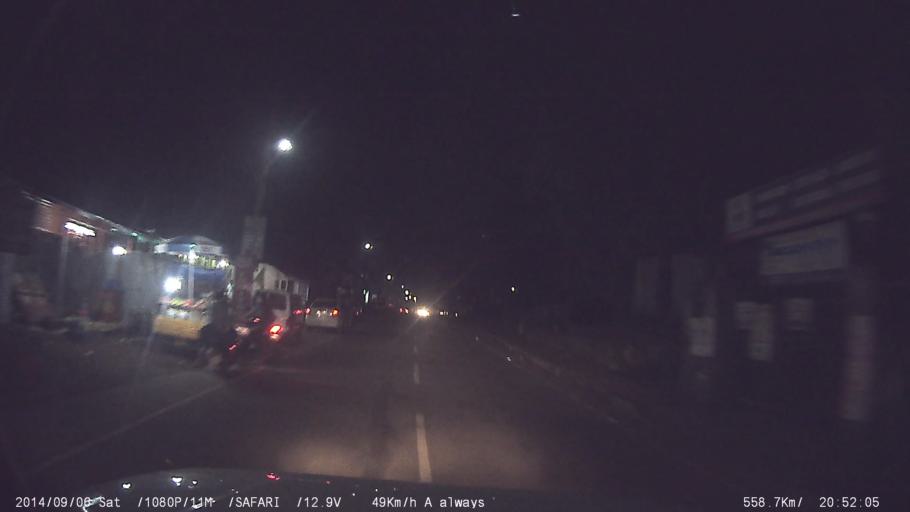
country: IN
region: Kerala
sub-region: Kottayam
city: Palackattumala
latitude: 9.7544
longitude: 76.5614
